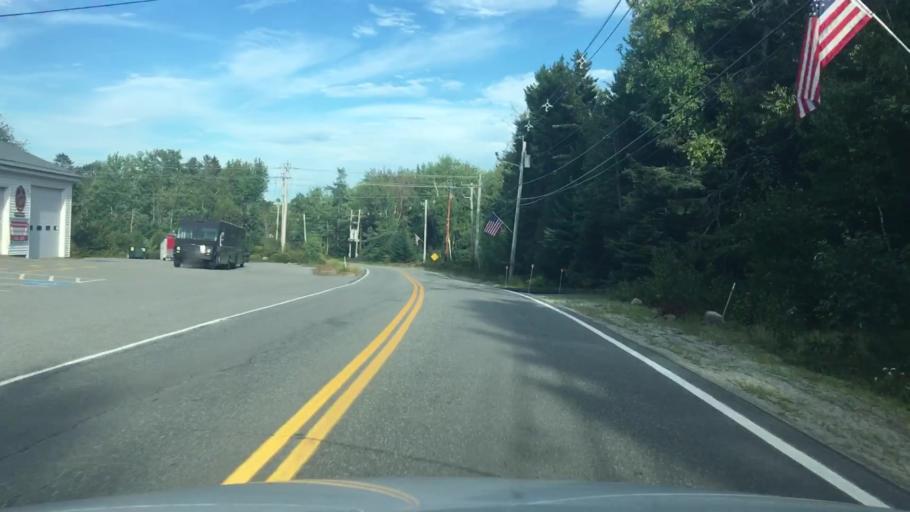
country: US
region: Maine
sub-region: Hancock County
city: Trenton
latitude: 44.4375
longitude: -68.3750
